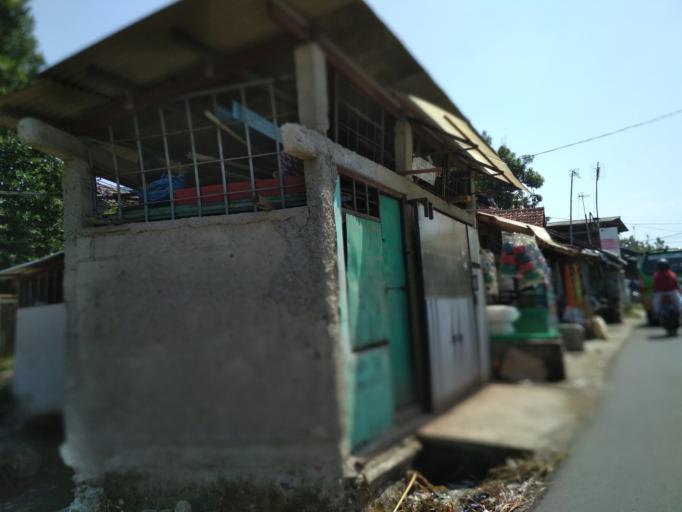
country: ID
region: West Java
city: Ciampea
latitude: -6.5551
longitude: 106.7452
